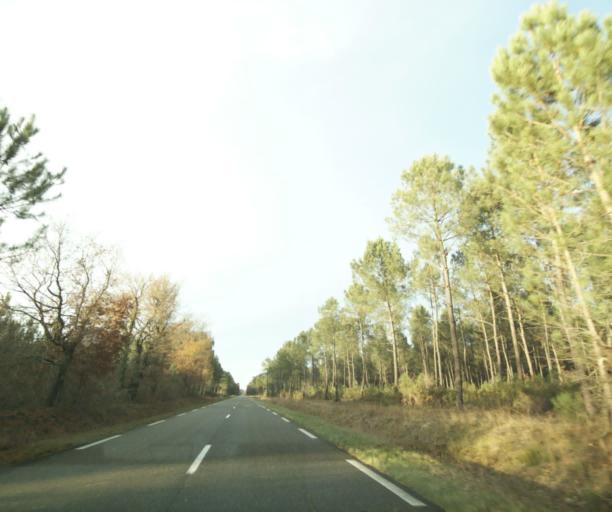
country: FR
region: Aquitaine
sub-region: Departement des Landes
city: Gabarret
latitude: 44.0389
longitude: -0.0345
